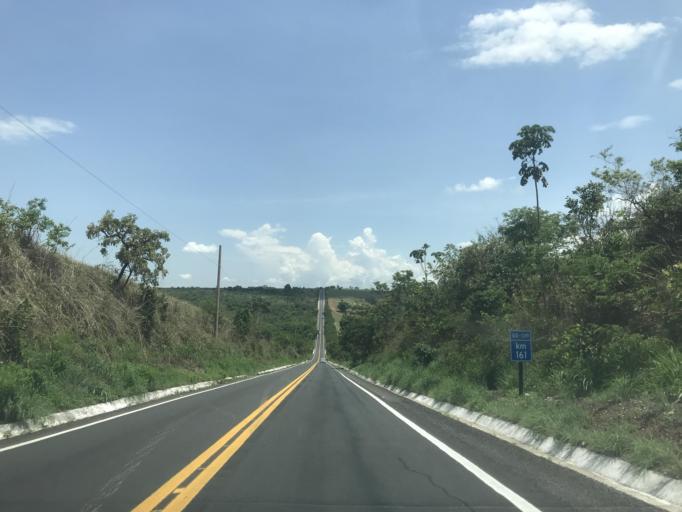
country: BR
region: Goias
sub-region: Bela Vista De Goias
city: Bela Vista de Goias
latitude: -17.1184
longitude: -48.6675
